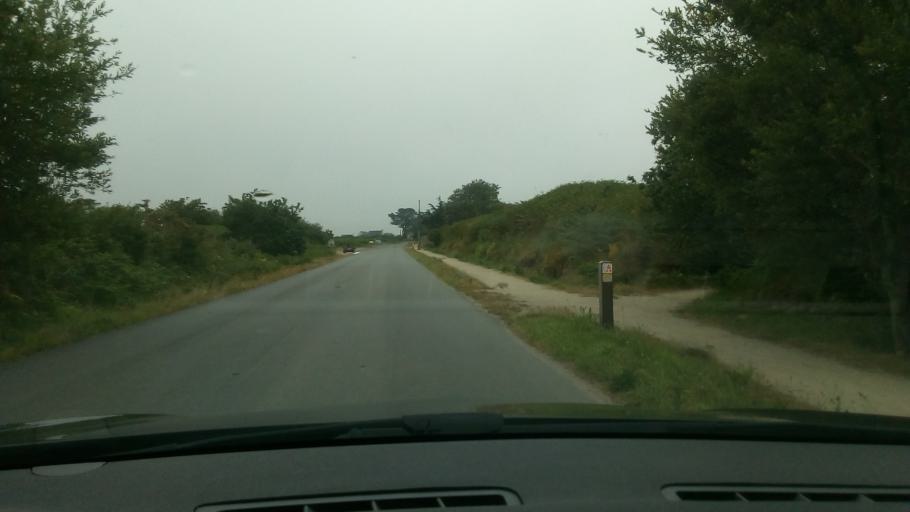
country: FR
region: Brittany
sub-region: Departement du Finistere
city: Le Conquet
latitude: 48.3720
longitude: -4.7533
